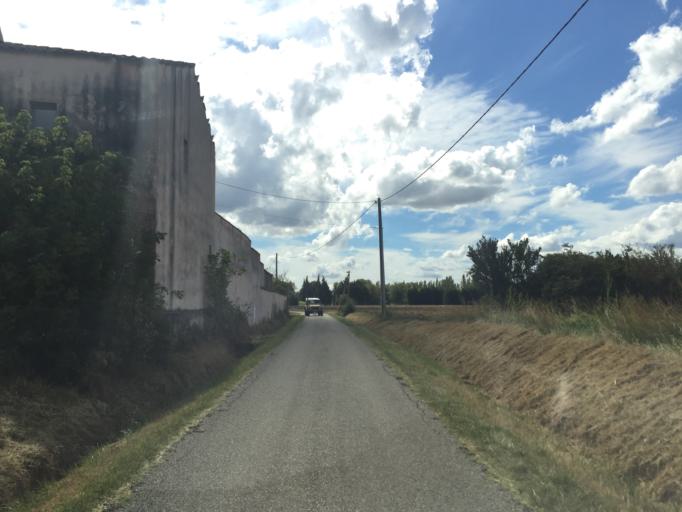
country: FR
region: Provence-Alpes-Cote d'Azur
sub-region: Departement du Vaucluse
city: Caderousse
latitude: 44.1087
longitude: 4.7687
